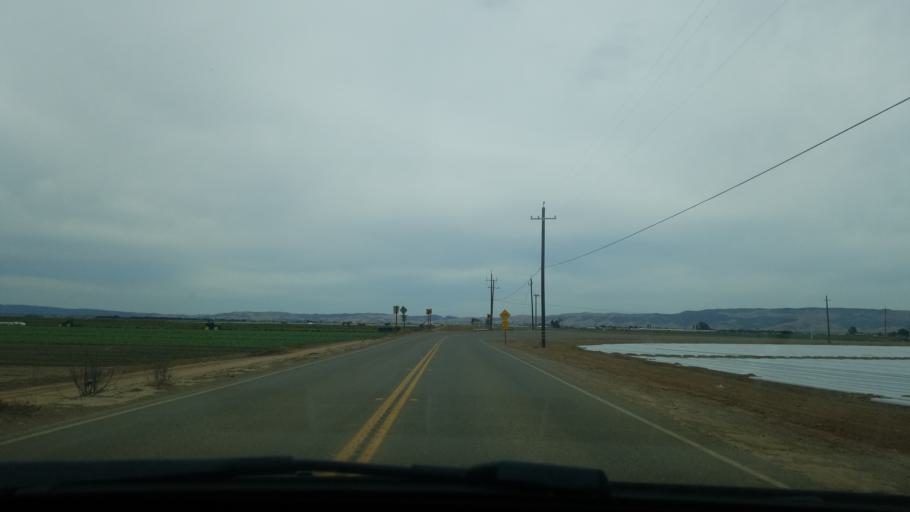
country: US
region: California
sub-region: San Luis Obispo County
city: Nipomo
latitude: 35.0082
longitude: -120.5021
